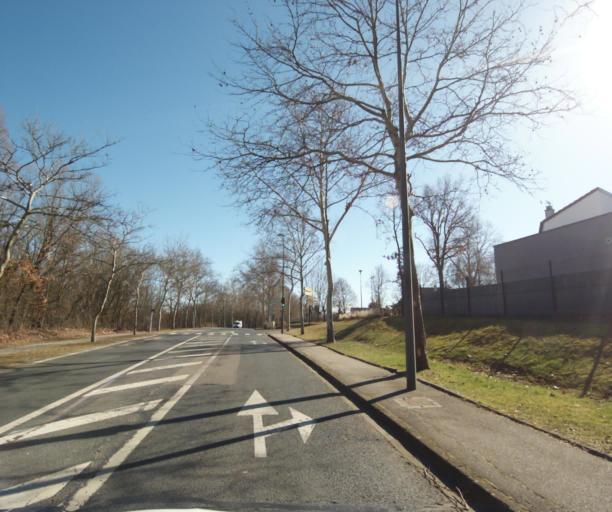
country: FR
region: Lorraine
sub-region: Departement de Meurthe-et-Moselle
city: Heillecourt
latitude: 48.6557
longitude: 6.2001
